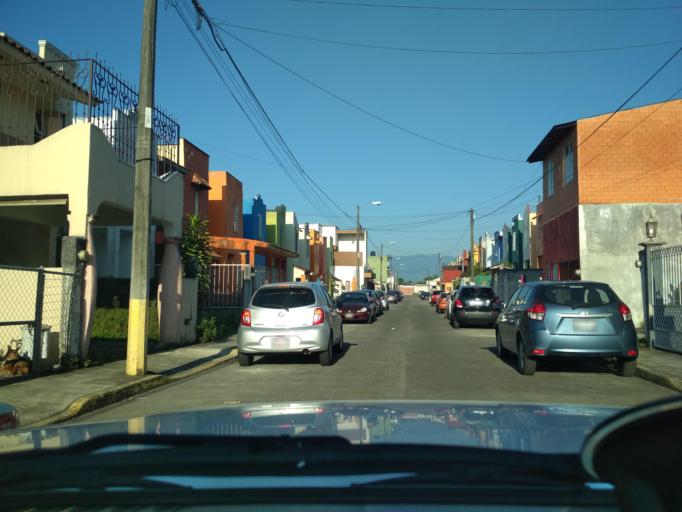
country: MX
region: Veracruz
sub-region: Fortin
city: Fraccionamiento Villas de la Llave
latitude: 18.9194
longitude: -96.9924
